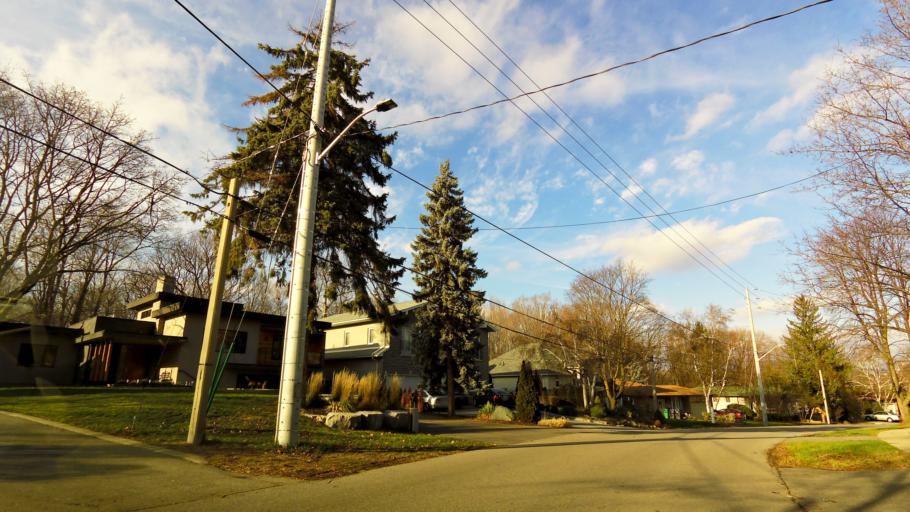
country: CA
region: Ontario
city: Mississauga
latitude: 43.5569
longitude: -79.6625
